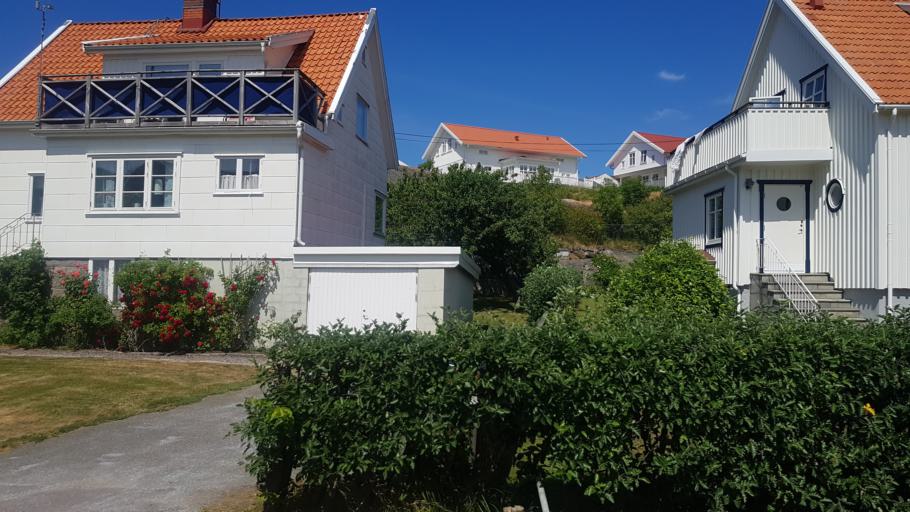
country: SE
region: Vaestra Goetaland
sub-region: Tjorns Kommun
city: Skaerhamn
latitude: 57.9960
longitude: 11.5562
